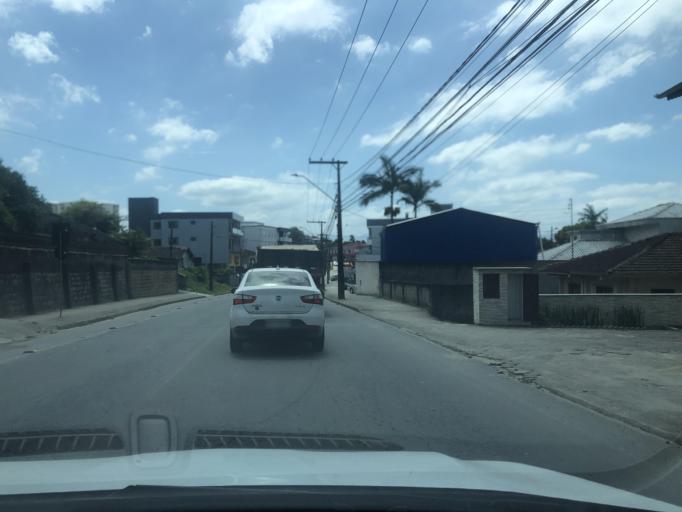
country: BR
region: Santa Catarina
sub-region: Joinville
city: Joinville
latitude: -26.3390
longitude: -48.8020
